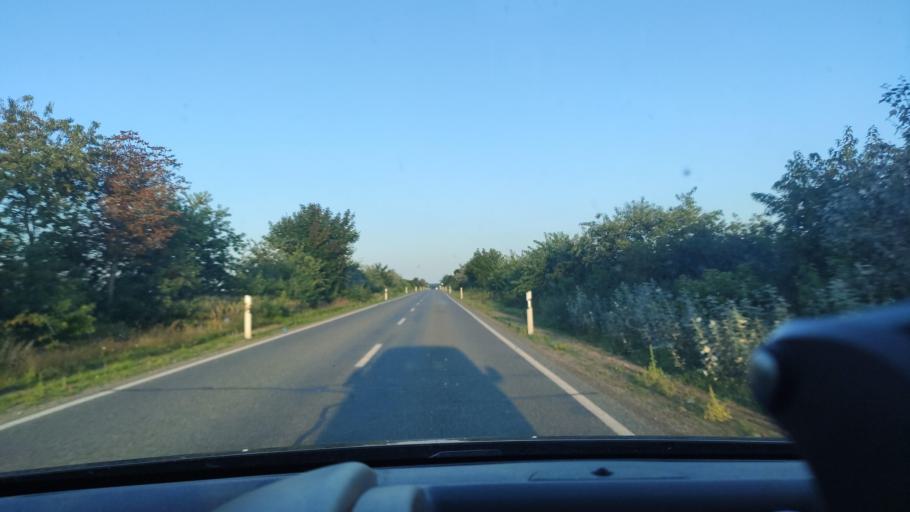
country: DE
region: Mecklenburg-Vorpommern
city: Krakow am See
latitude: 53.6166
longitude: 12.3836
